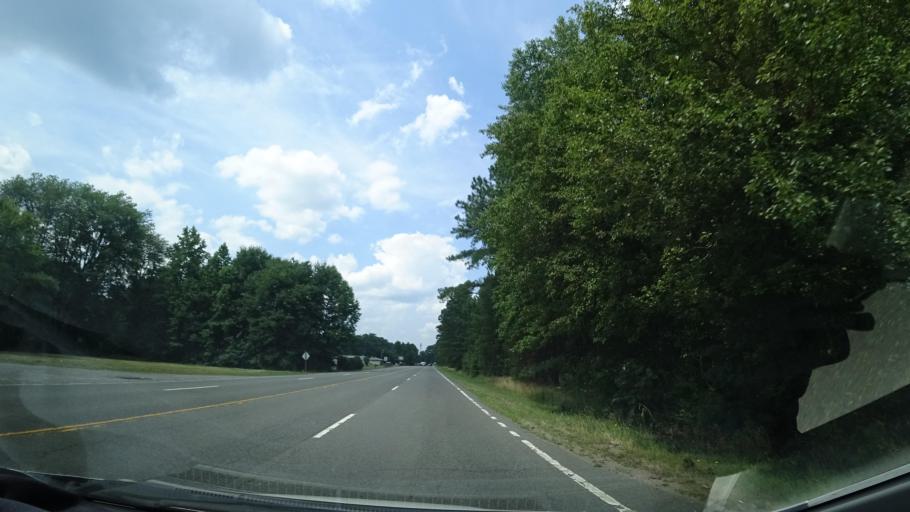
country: US
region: Virginia
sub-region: Hanover County
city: Ashland
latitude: 37.7720
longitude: -77.4684
